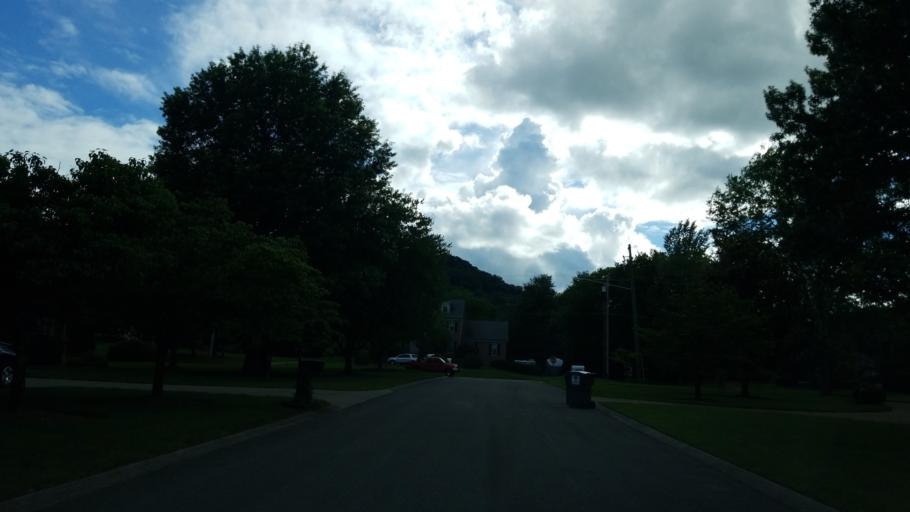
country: US
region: Tennessee
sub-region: Davidson County
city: Forest Hills
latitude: 36.0279
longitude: -86.8283
